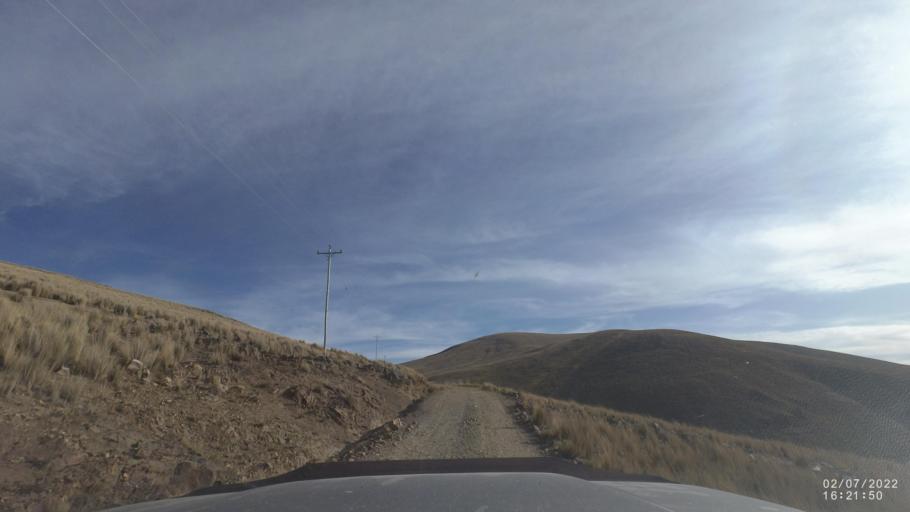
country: BO
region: Cochabamba
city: Irpa Irpa
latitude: -17.9324
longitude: -66.4534
